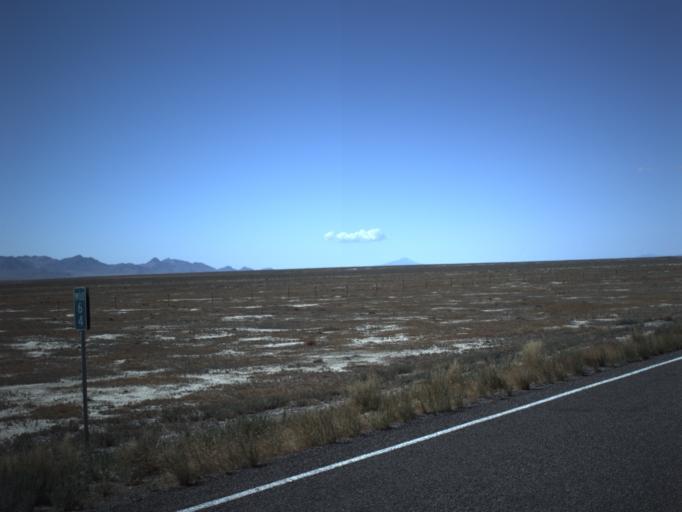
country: US
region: Utah
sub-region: Millard County
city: Delta
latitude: 39.2059
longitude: -112.9739
